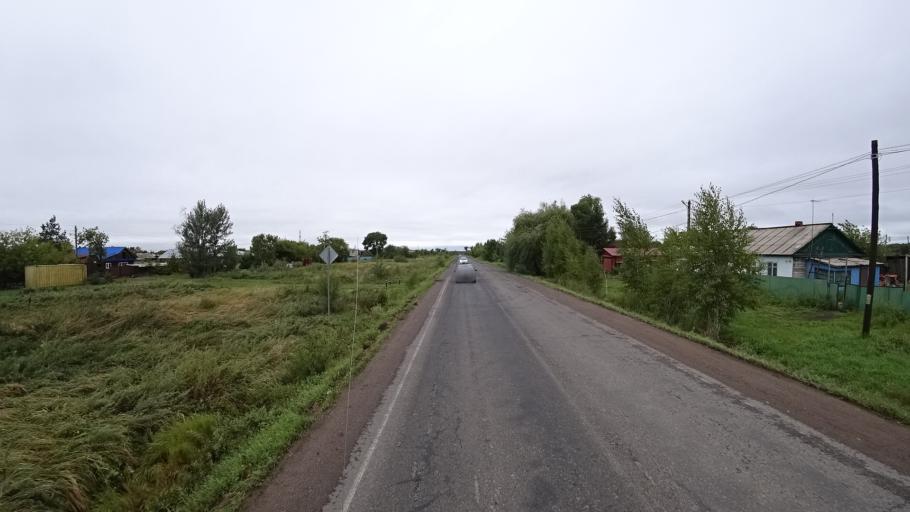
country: RU
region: Primorskiy
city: Monastyrishche
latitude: 44.1966
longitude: 132.4789
